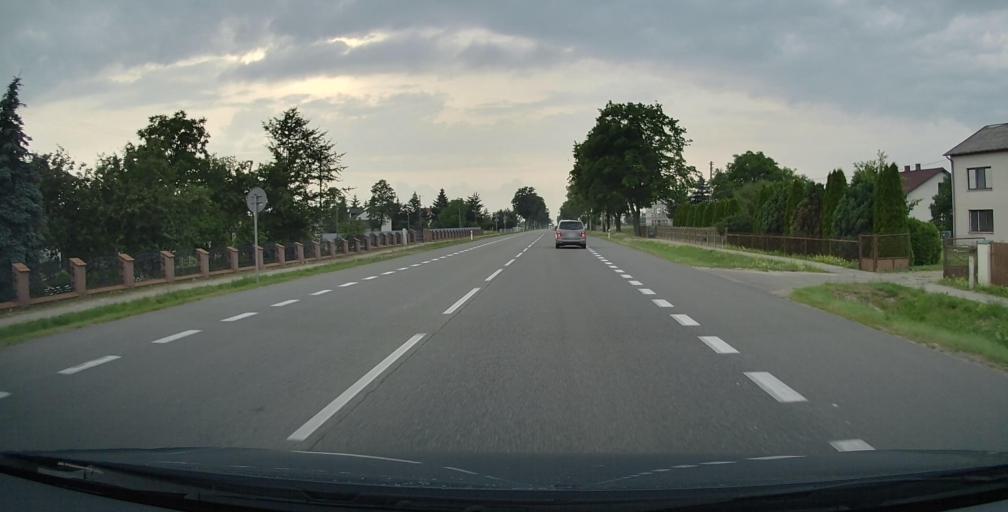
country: PL
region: Masovian Voivodeship
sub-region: Powiat siedlecki
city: Zbuczyn
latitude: 52.1093
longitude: 22.3840
